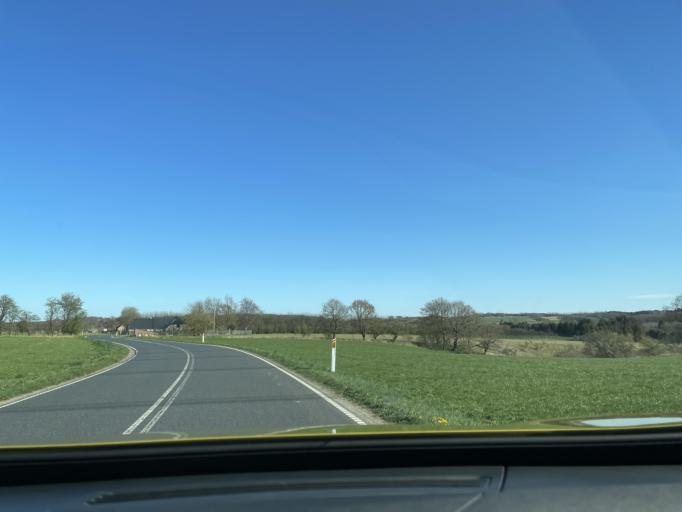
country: DK
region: Central Jutland
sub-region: Silkeborg Kommune
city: Kjellerup
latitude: 56.2507
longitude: 9.4462
